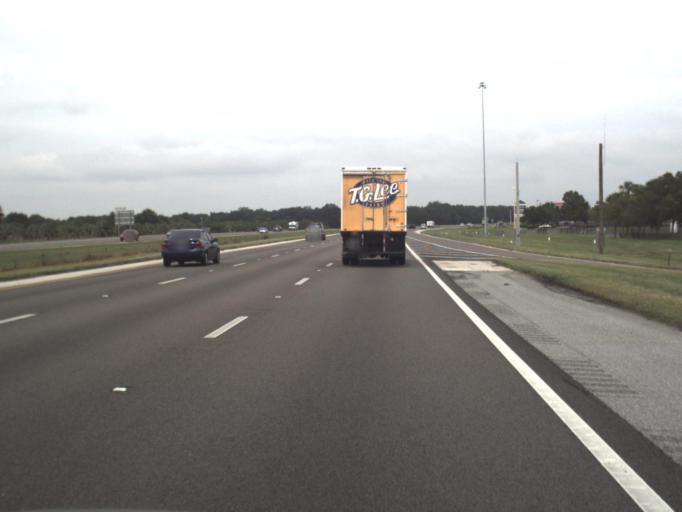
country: US
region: Florida
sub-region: Manatee County
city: Ellenton
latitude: 27.5329
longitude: -82.5091
